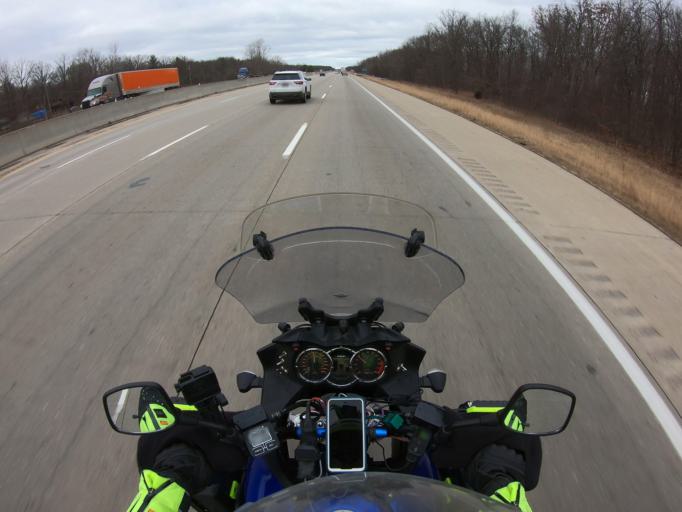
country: US
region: Michigan
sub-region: Saginaw County
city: Birch Run
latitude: 43.2723
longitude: -83.8015
